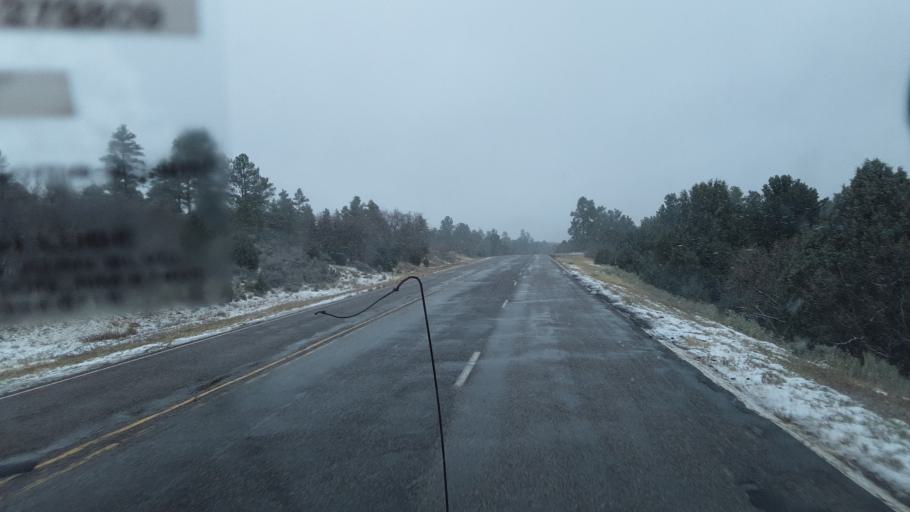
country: US
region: New Mexico
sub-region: Rio Arriba County
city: Tierra Amarilla
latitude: 36.6672
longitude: -106.5571
